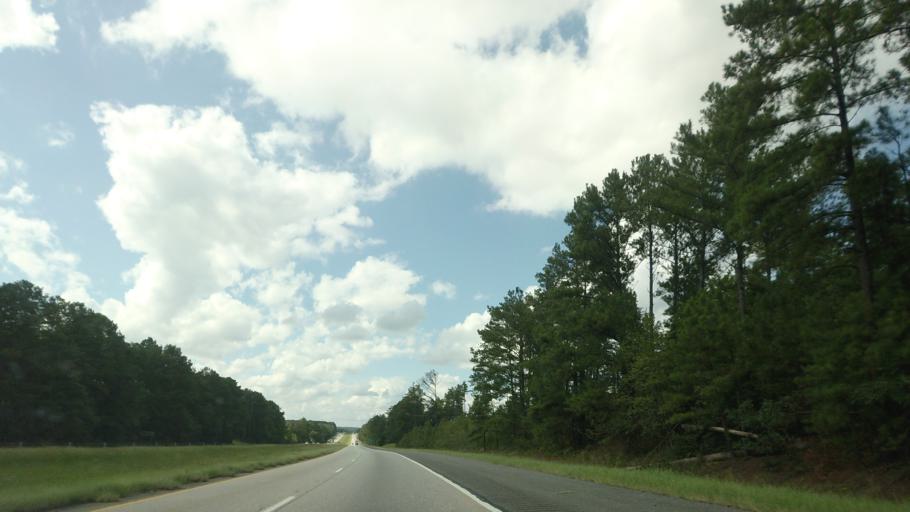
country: US
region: Georgia
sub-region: Bibb County
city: Macon
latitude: 32.7864
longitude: -83.5600
